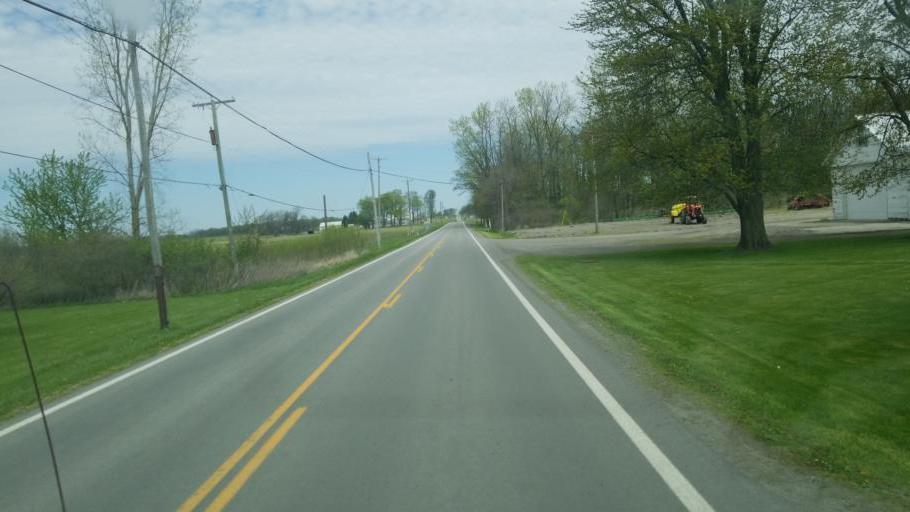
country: US
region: Ohio
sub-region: Hardin County
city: Ada
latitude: 40.6954
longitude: -83.7852
